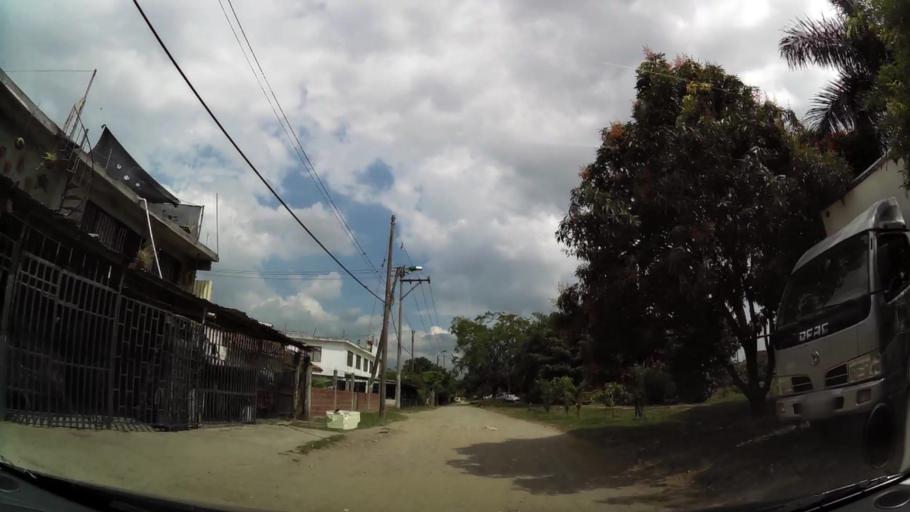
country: CO
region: Valle del Cauca
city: Cali
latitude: 3.4856
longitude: -76.4854
